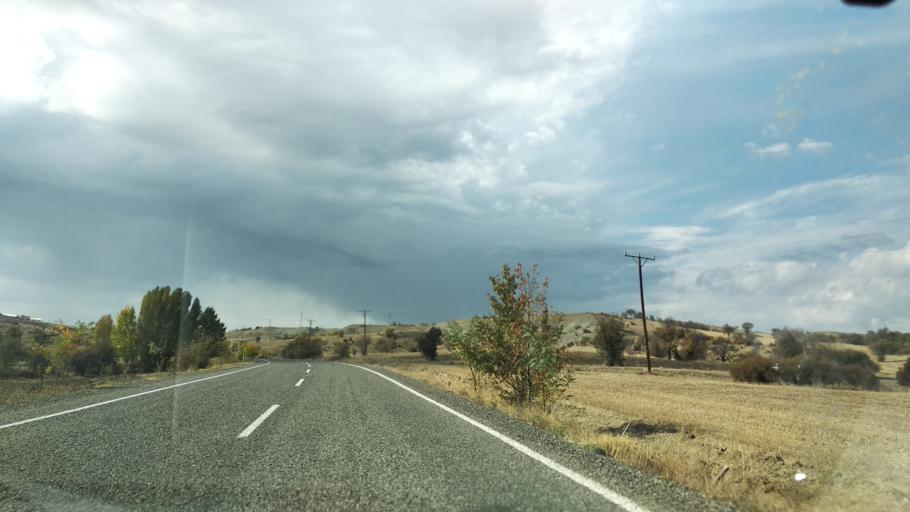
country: TR
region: Bolu
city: Seben
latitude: 40.3822
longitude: 31.5265
